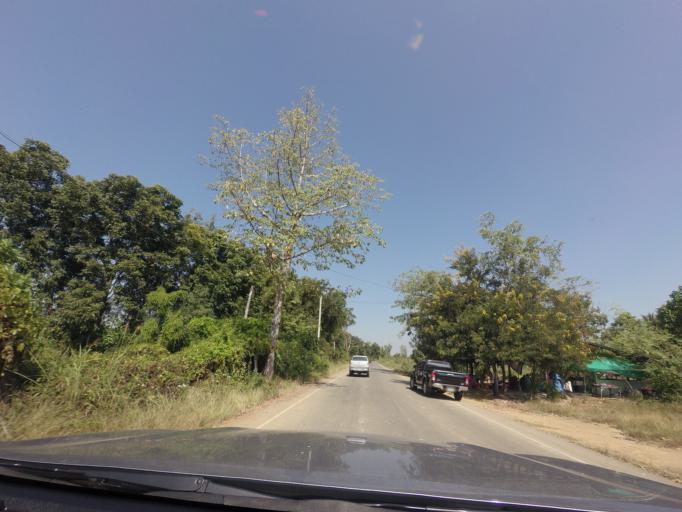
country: TH
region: Sukhothai
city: Si Samrong
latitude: 17.1259
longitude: 99.7817
